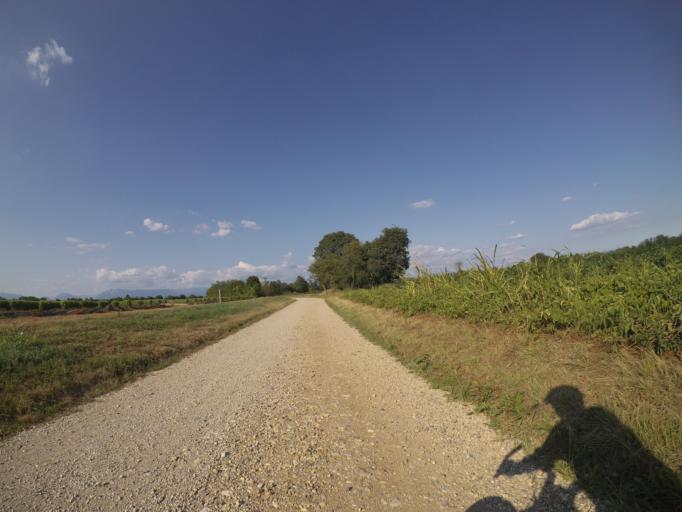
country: IT
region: Friuli Venezia Giulia
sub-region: Provincia di Udine
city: Pozzuolo del Friuli
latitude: 46.0019
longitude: 13.1830
